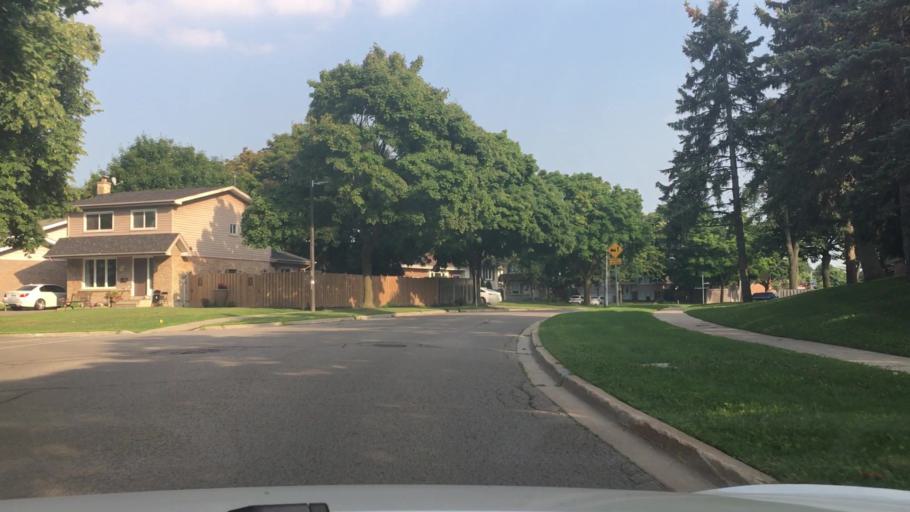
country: CA
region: Ontario
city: Ajax
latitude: 43.8740
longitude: -78.9543
